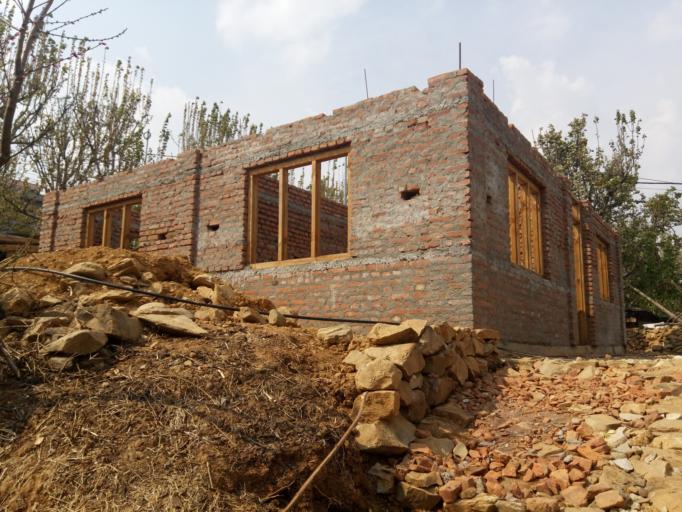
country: NP
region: Central Region
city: Kirtipur
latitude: 27.5945
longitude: 85.2624
